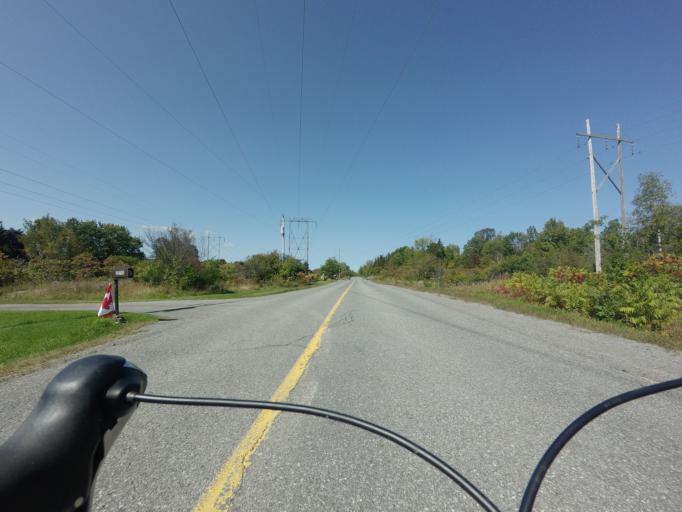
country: CA
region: Ontario
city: Bells Corners
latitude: 45.3838
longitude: -76.0191
